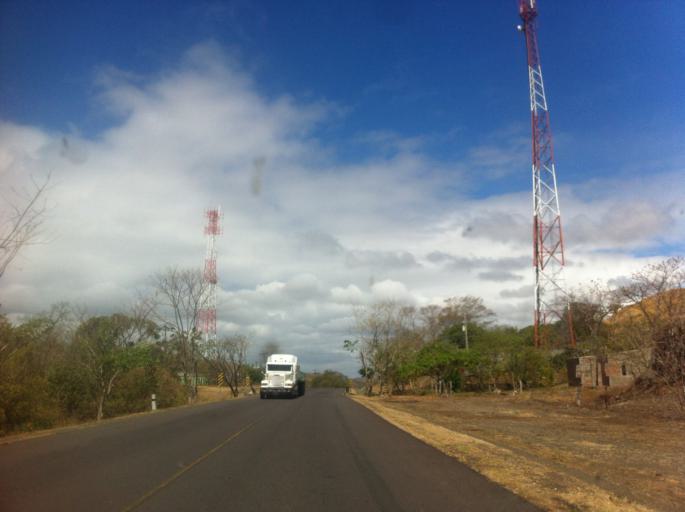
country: NI
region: Chontales
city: Acoyapa
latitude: 12.0188
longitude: -85.2514
